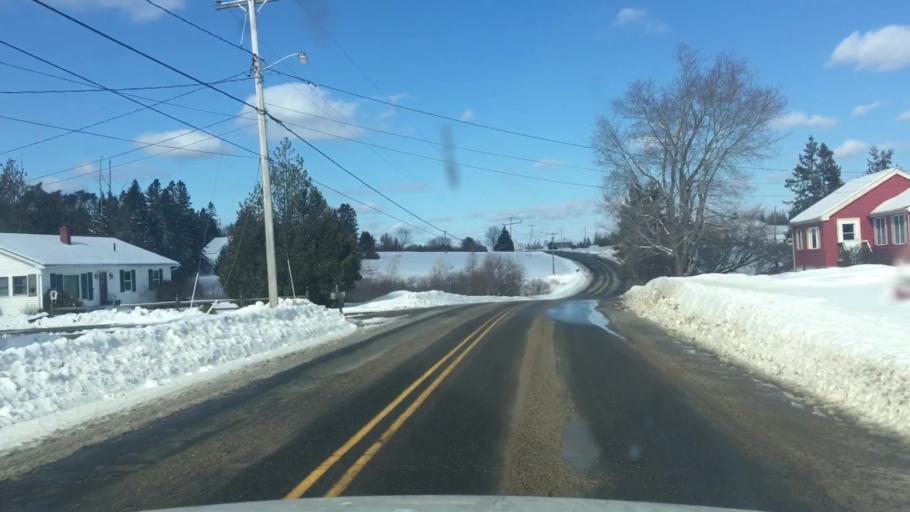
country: US
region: Maine
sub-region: Washington County
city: Machias
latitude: 44.6947
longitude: -67.4675
